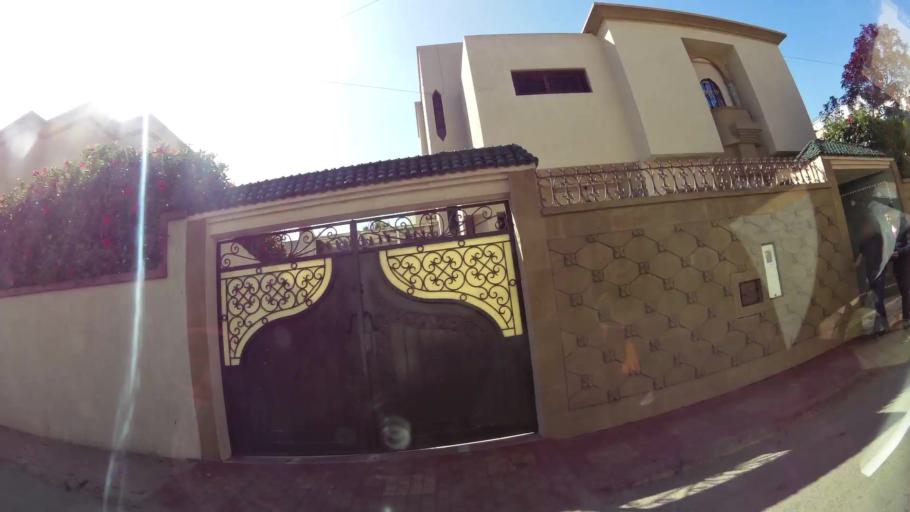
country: MA
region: Rabat-Sale-Zemmour-Zaer
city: Sale
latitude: 34.0655
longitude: -6.7964
